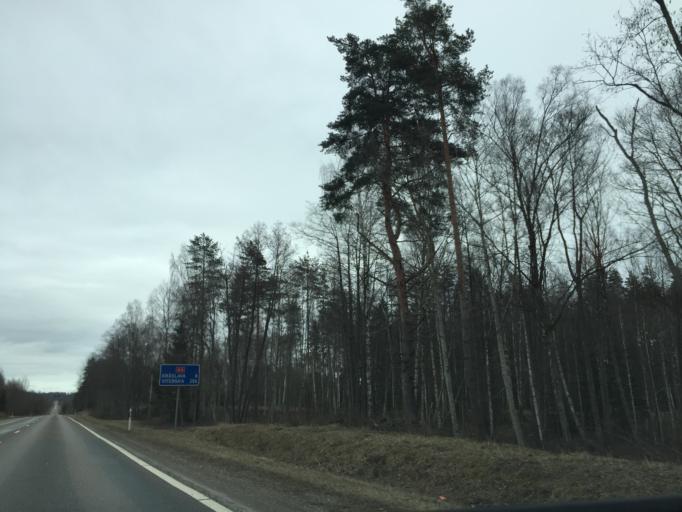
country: LV
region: Kraslavas Rajons
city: Kraslava
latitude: 55.9130
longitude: 27.0482
